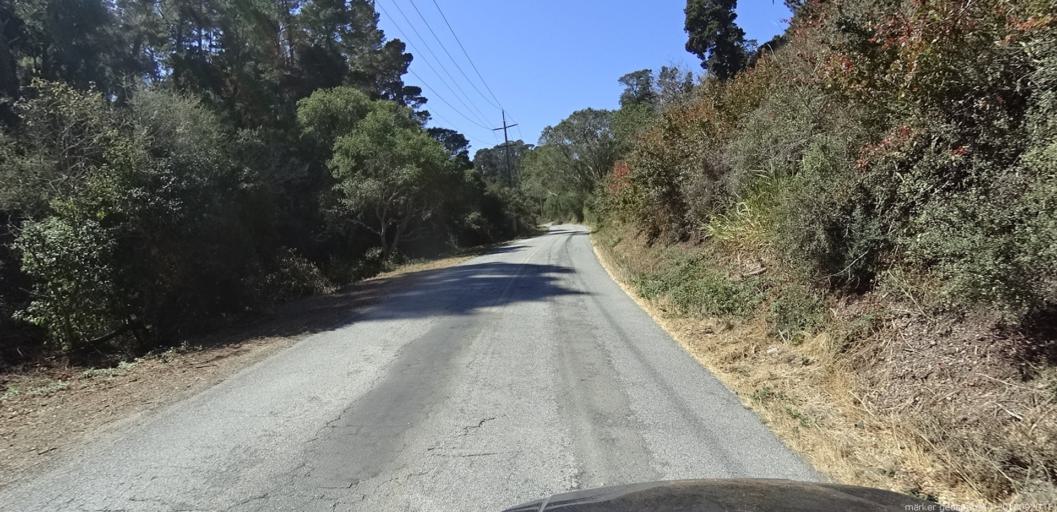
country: US
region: California
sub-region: Monterey County
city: Monterey
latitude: 36.5736
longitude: -121.8754
